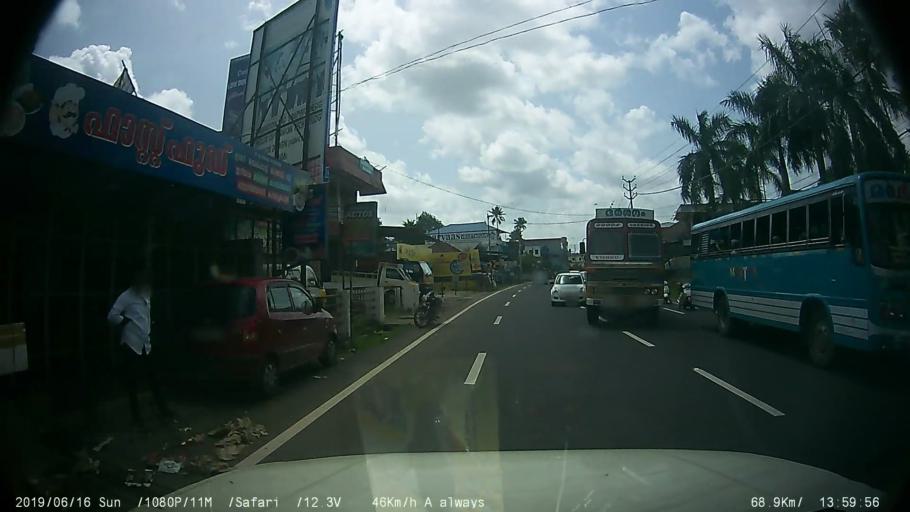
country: IN
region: Kerala
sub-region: Ernakulam
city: Muvattupula
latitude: 10.0070
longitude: 76.5689
